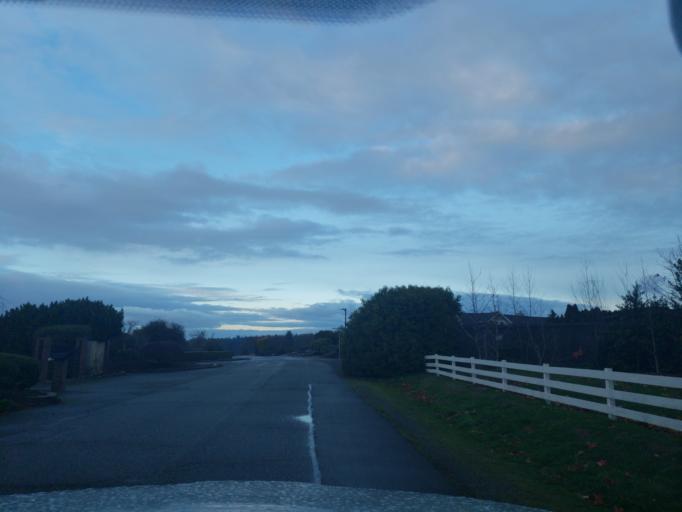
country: US
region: Washington
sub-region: King County
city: Shoreline
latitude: 47.7529
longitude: -122.3748
